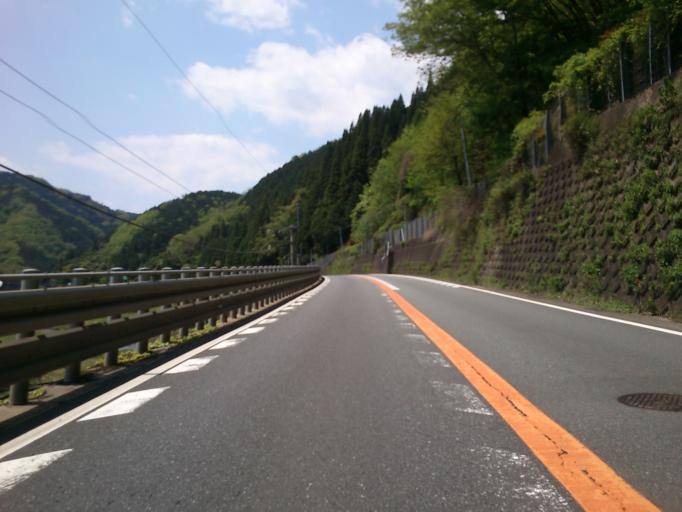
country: JP
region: Kyoto
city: Fukuchiyama
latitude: 35.3212
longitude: 134.9924
